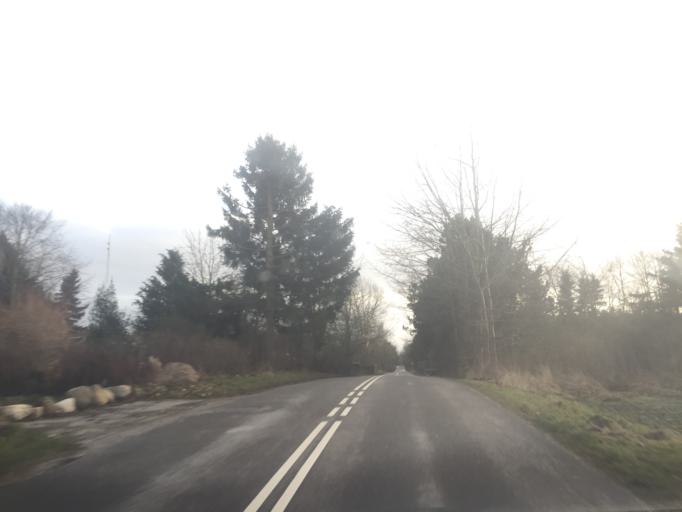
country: DK
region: Capital Region
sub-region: Egedal Kommune
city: Smorumnedre
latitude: 55.7143
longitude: 12.2660
